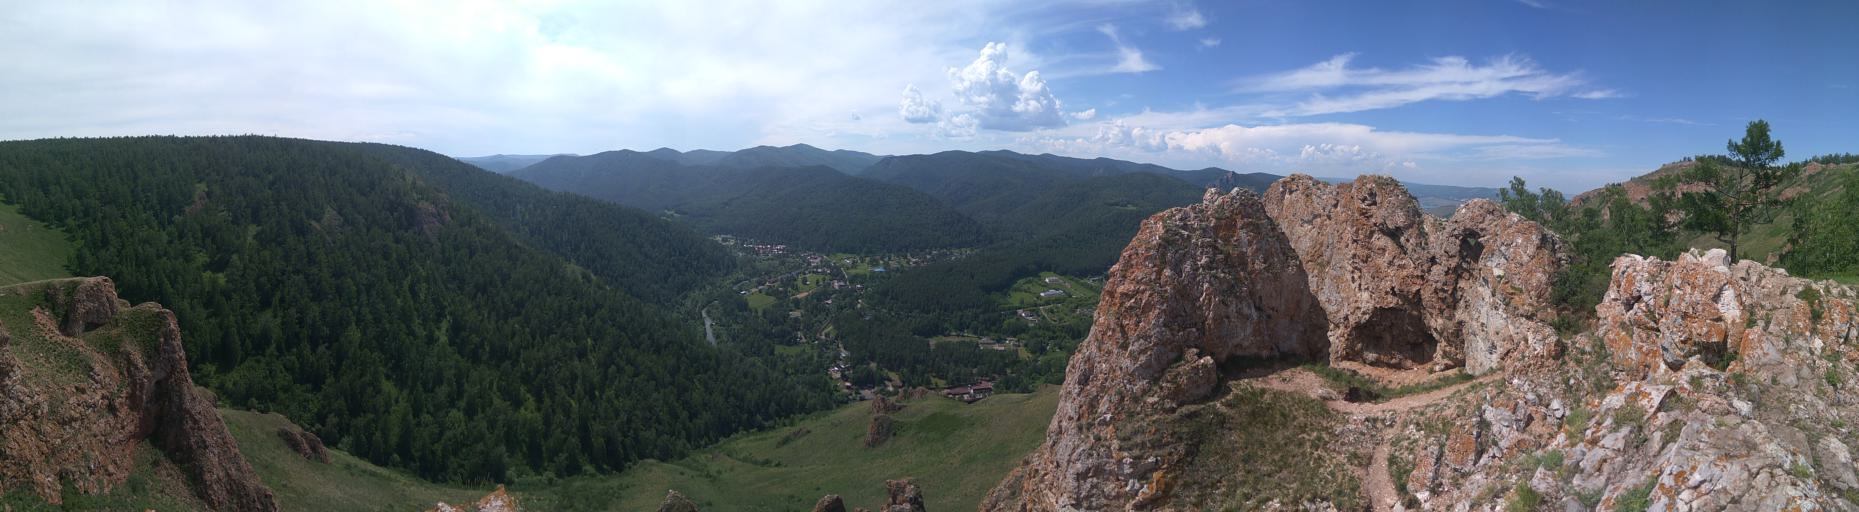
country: RU
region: Krasnoyarskiy
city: Krasnoyarsk
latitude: 55.9490
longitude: 92.8588
